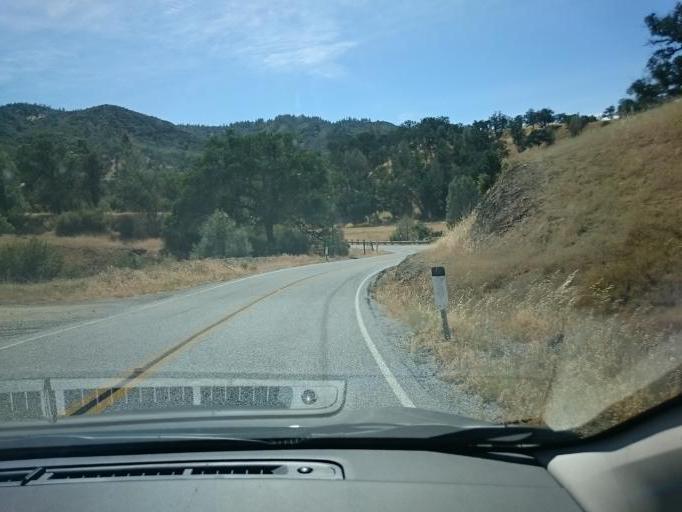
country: US
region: California
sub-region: Santa Clara County
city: East Foothills
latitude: 37.3567
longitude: -121.5885
